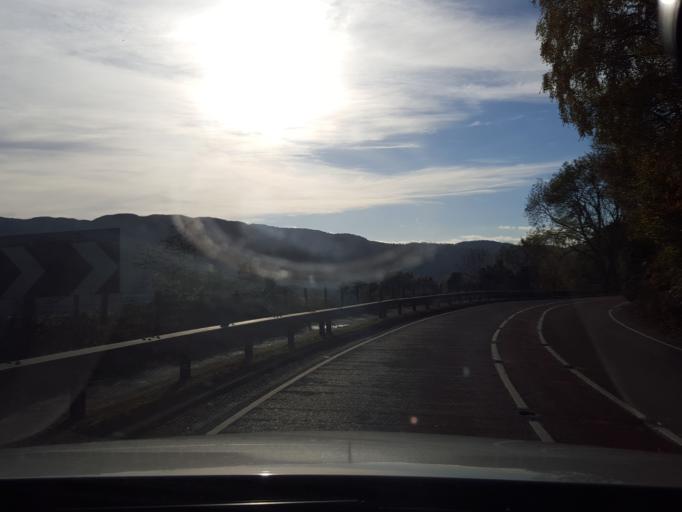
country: GB
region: Scotland
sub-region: Highland
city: Beauly
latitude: 57.3268
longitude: -4.4452
